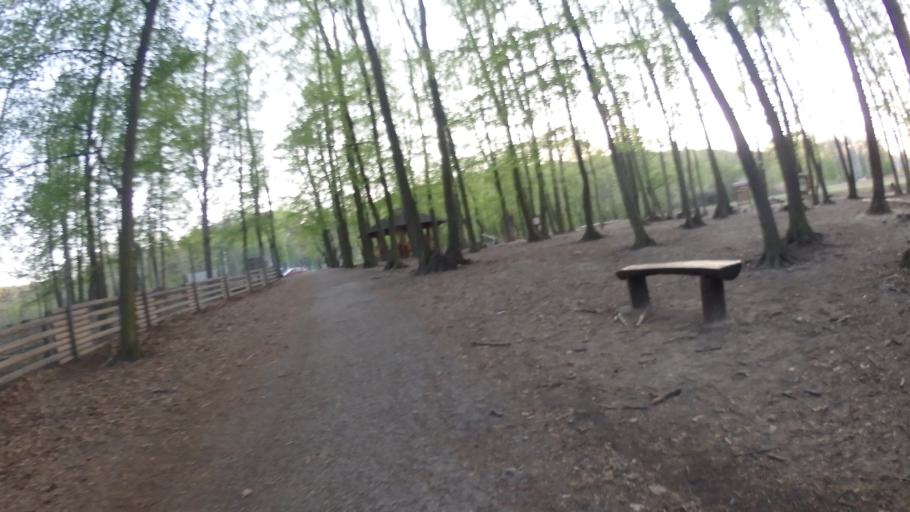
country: CZ
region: South Moravian
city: Troubsko
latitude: 49.2004
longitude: 16.5187
